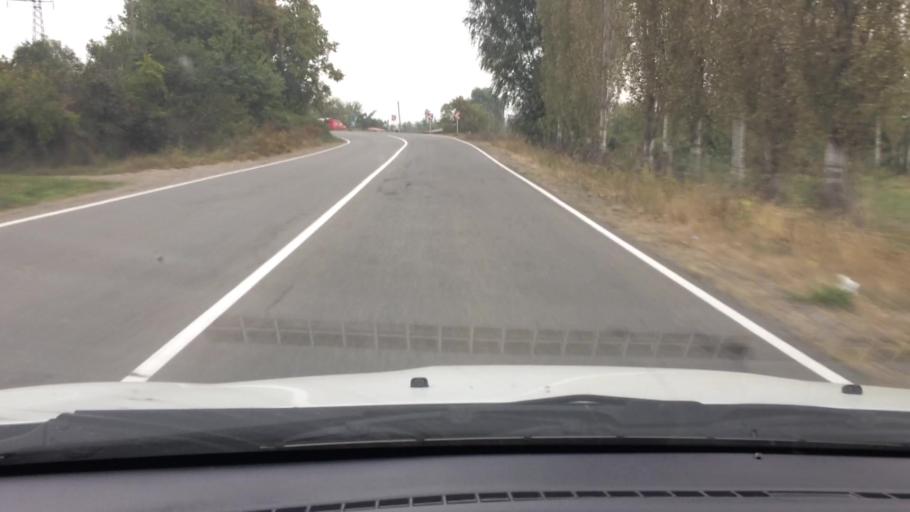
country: GE
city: Naghvarevi
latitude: 41.3054
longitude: 44.7907
